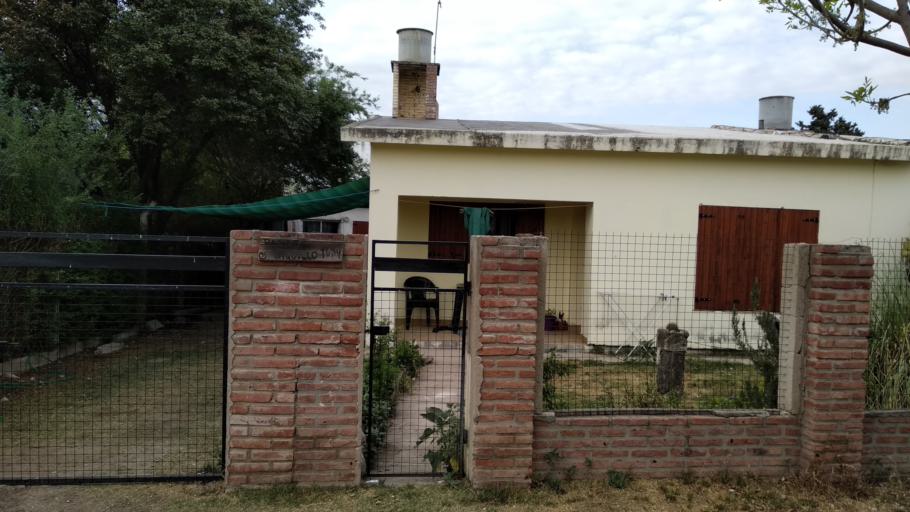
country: AR
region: Cordoba
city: Mina Clavero
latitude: -31.7305
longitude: -65.0114
